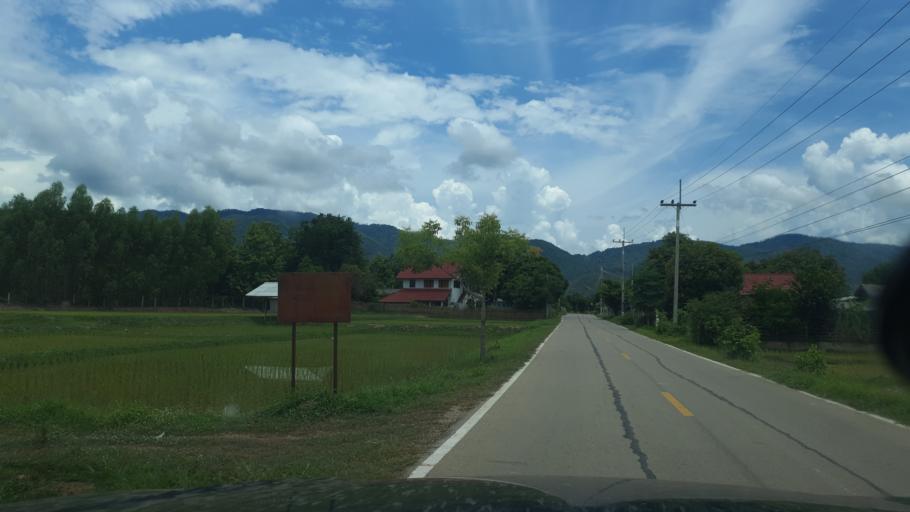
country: TH
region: Lampang
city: Sop Prap
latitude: 17.9129
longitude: 99.4123
